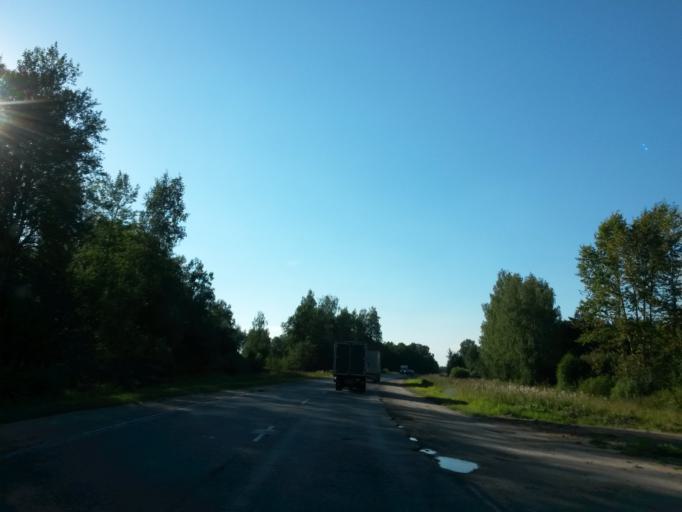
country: RU
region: Ivanovo
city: Novo-Talitsy
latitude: 57.0687
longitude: 40.6948
